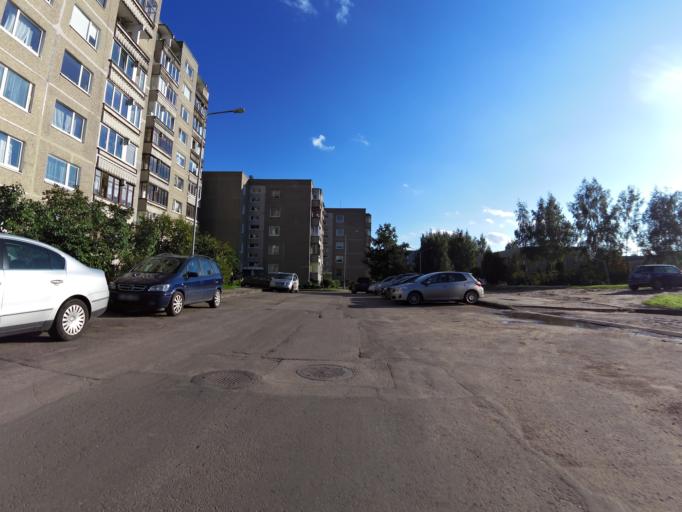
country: LT
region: Vilnius County
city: Justiniskes
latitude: 54.7142
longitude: 25.2130
